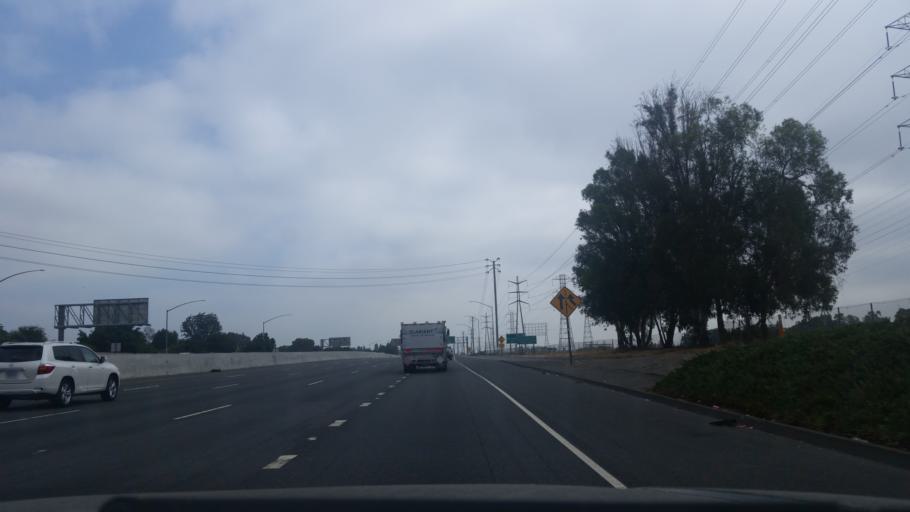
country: US
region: California
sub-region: Los Angeles County
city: East Rancho Dominguez
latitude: 33.8635
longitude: -118.1984
